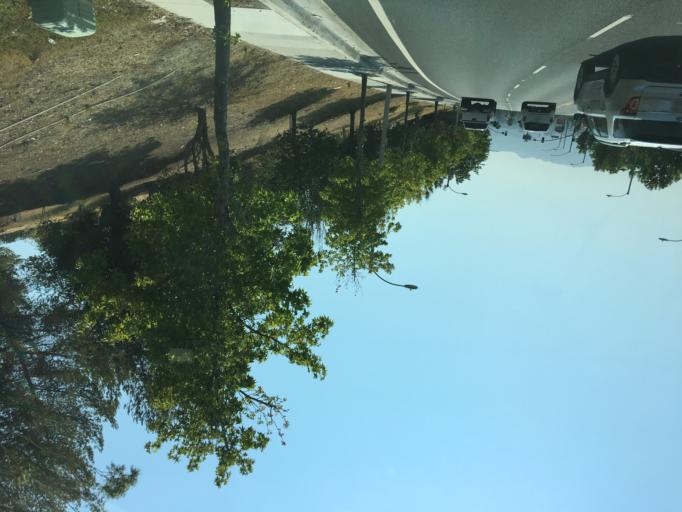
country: US
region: California
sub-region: Los Angeles County
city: Santa Clarita
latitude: 34.3785
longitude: -118.5696
